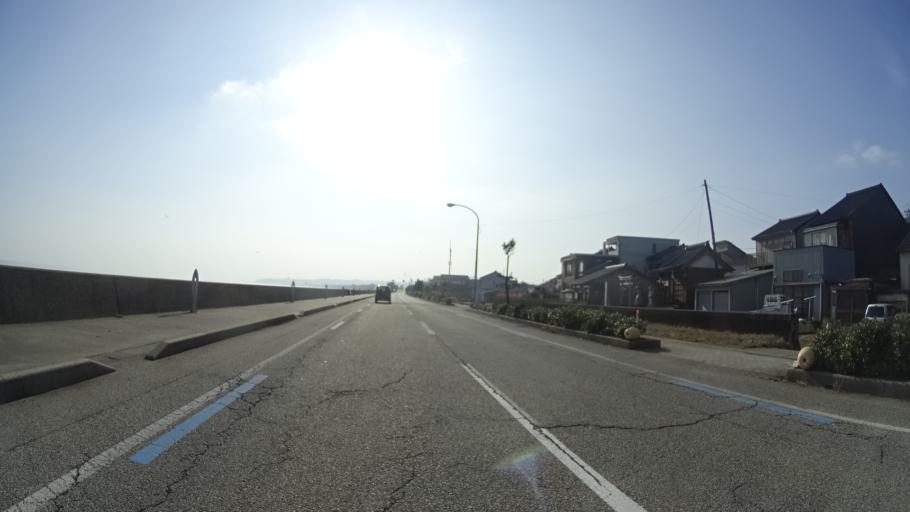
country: JP
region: Toyama
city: Himi
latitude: 36.8518
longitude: 136.9925
